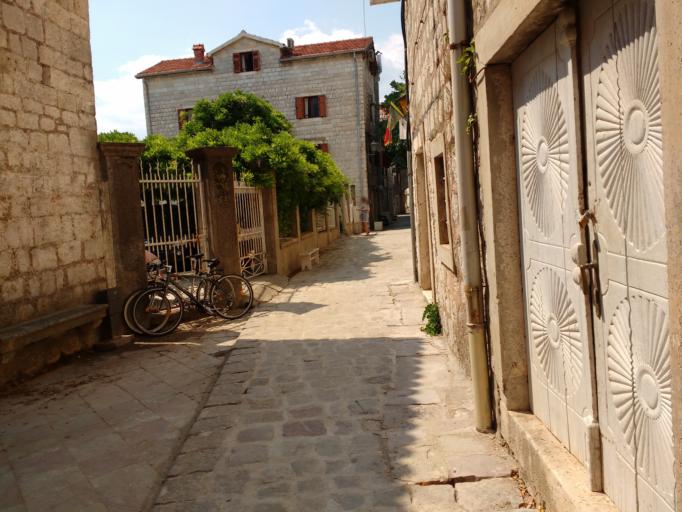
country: ME
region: Kotor
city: Risan
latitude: 42.4853
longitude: 18.7003
